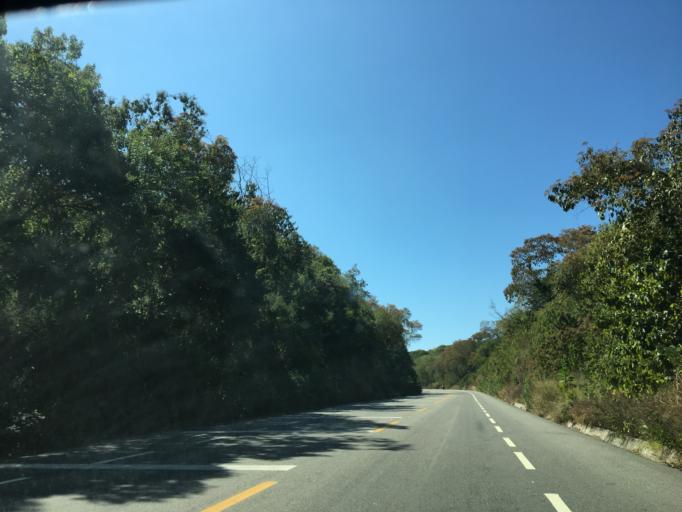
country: MX
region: Oaxaca
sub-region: Santa Maria Huatulco
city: Sector H Tres
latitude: 15.7783
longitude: -96.2168
